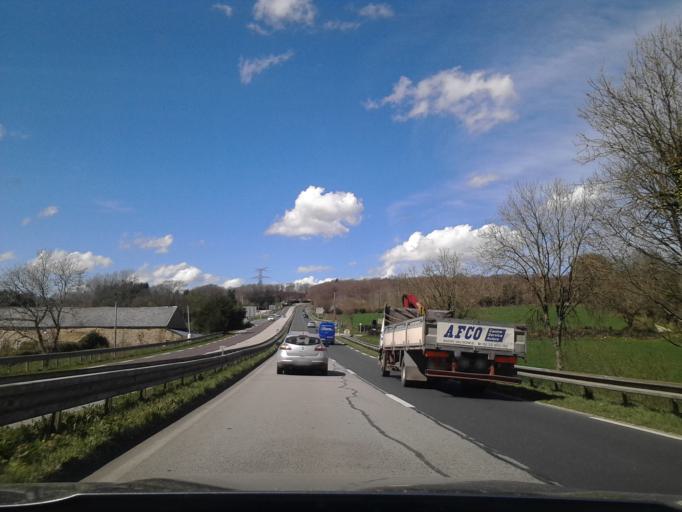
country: FR
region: Lower Normandy
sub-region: Departement de la Manche
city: Brix
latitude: 49.5435
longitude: -1.5513
